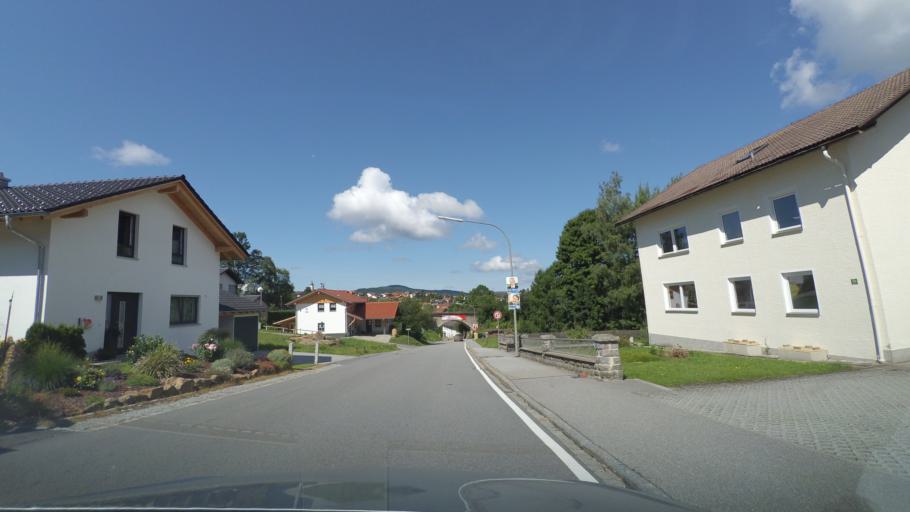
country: DE
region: Bavaria
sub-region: Lower Bavaria
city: Bodenmais
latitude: 49.0674
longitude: 13.1093
